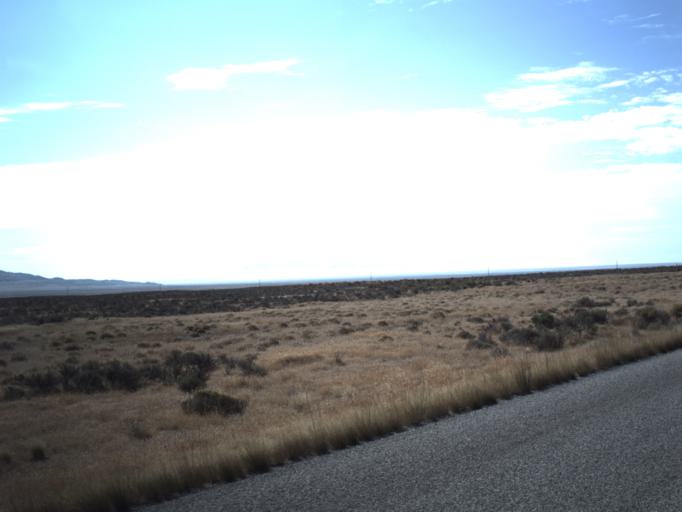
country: US
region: Utah
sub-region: Tooele County
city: Wendover
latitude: 41.5450
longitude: -113.5888
